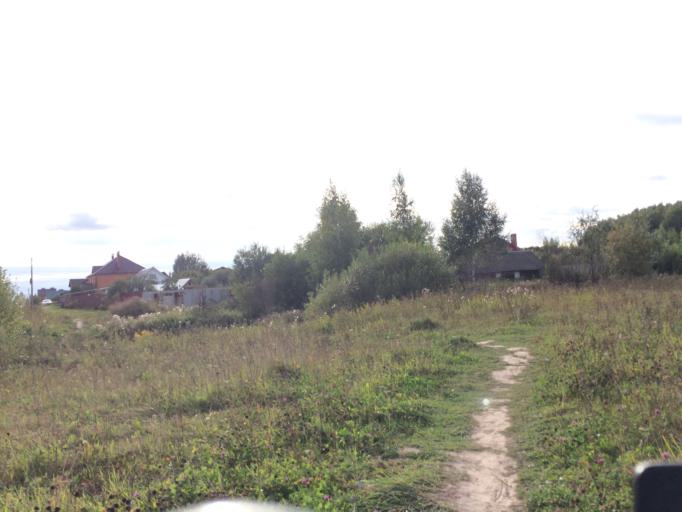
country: RU
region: Mariy-El
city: Yoshkar-Ola
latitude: 56.6546
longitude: 47.9940
